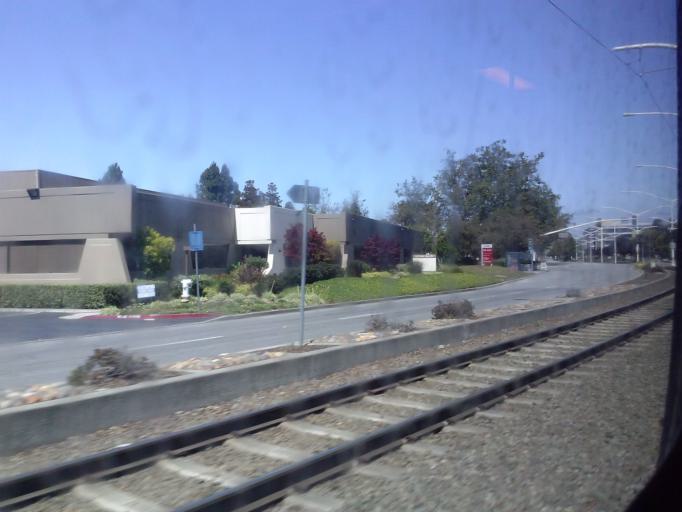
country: US
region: California
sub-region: Santa Clara County
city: Sunnyvale
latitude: 37.4104
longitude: -122.0128
